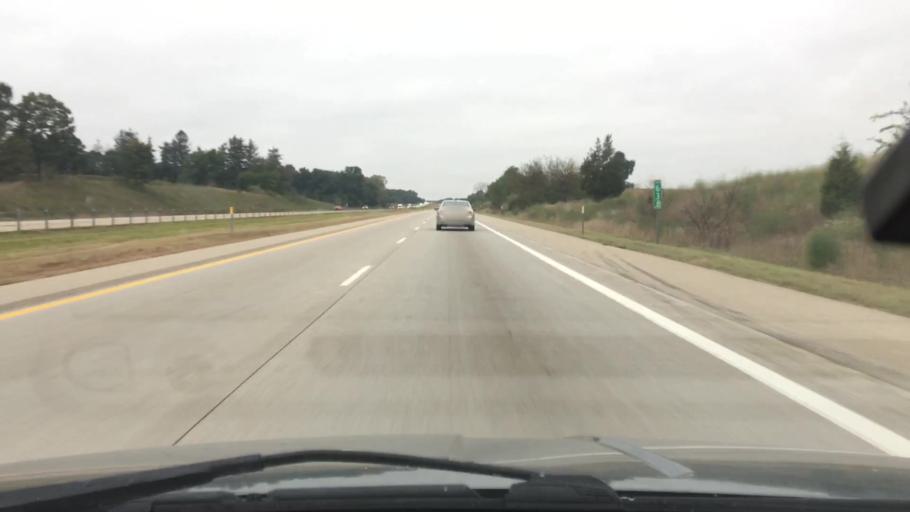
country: US
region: Michigan
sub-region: Van Buren County
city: Mattawan
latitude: 42.2201
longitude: -85.8246
